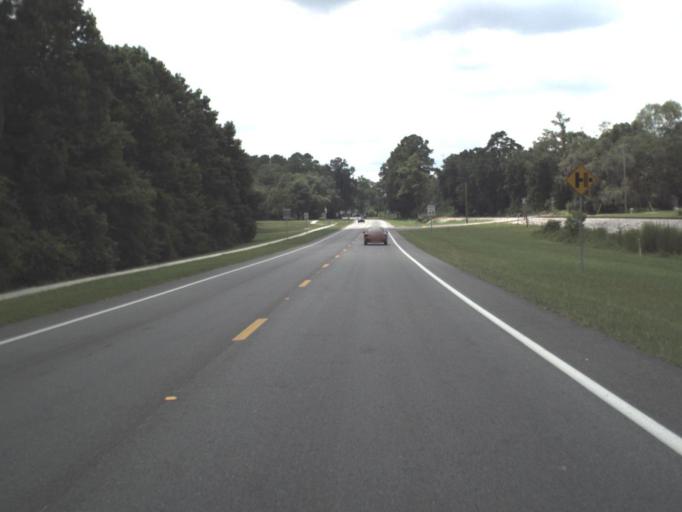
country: US
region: Florida
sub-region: Suwannee County
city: Wellborn
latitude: 30.3271
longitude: -82.7408
